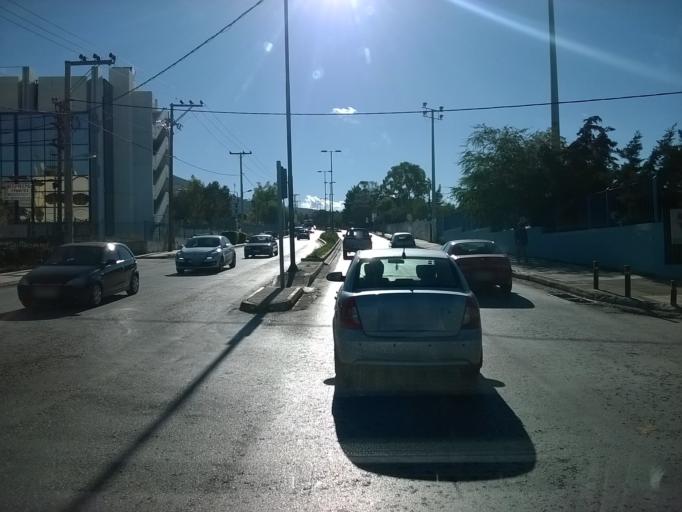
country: GR
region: Attica
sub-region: Nomarchia Athinas
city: Argyroupoli
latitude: 37.8987
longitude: 23.7574
